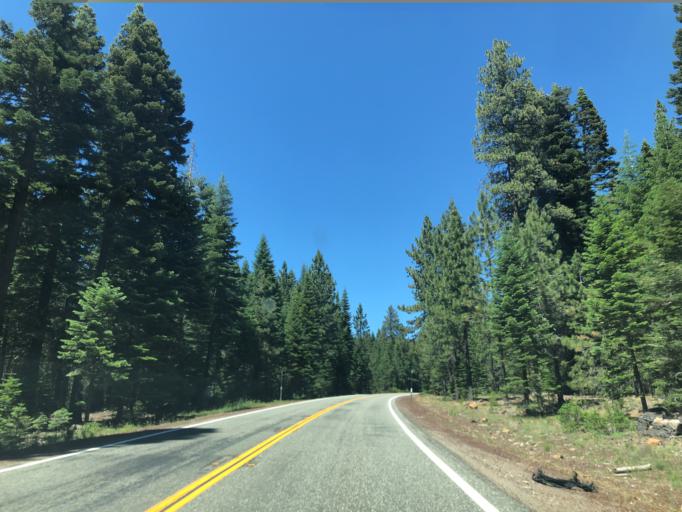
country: US
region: California
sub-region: Shasta County
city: Shingletown
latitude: 40.5519
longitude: -121.5801
